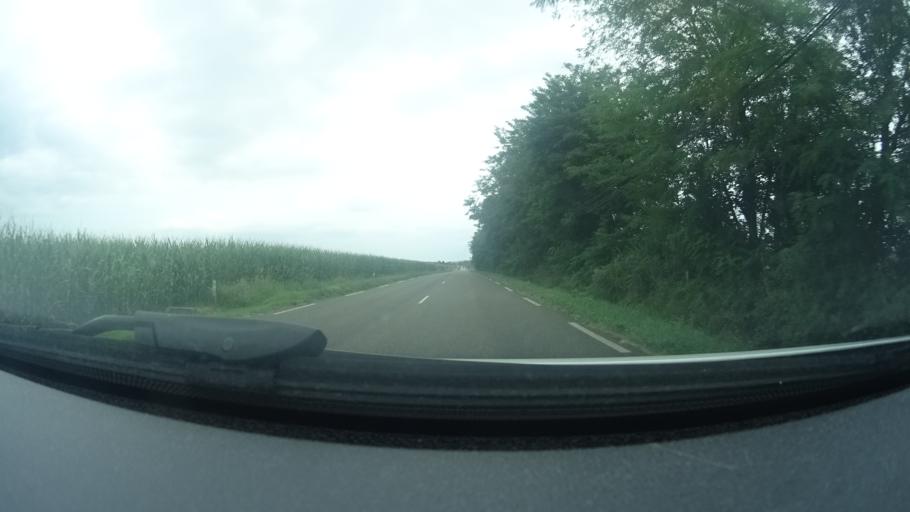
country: FR
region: Aquitaine
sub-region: Departement des Pyrenees-Atlantiques
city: Mont
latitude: 43.4493
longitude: -0.7025
